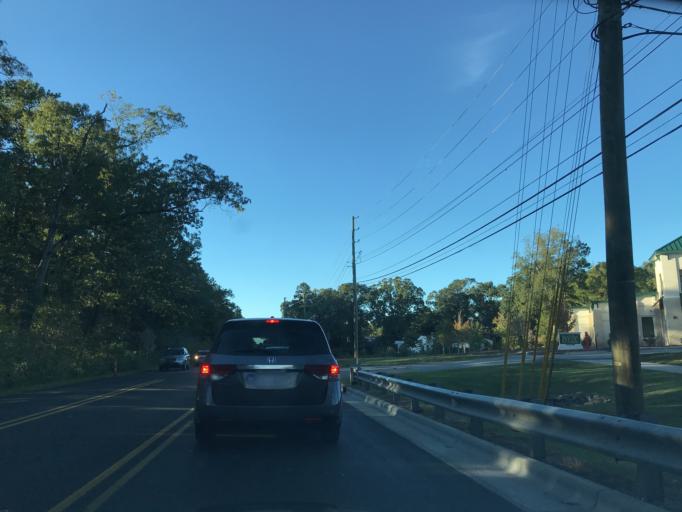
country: US
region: North Carolina
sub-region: Wake County
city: Morrisville
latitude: 35.8379
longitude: -78.8302
